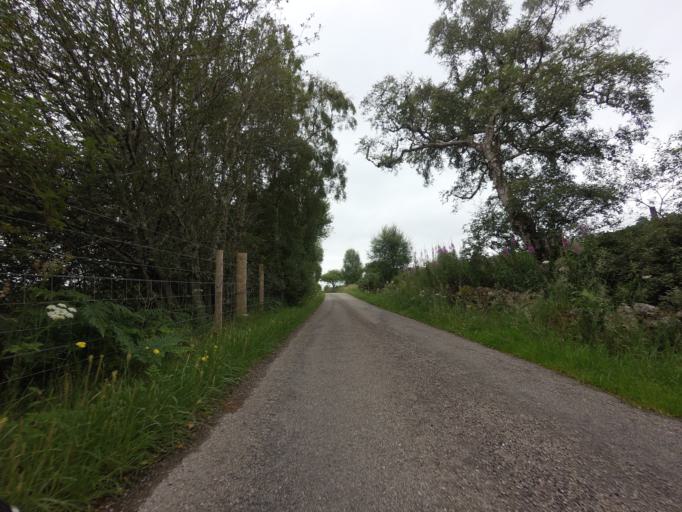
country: GB
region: Scotland
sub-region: Highland
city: Evanton
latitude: 57.9093
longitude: -4.3972
